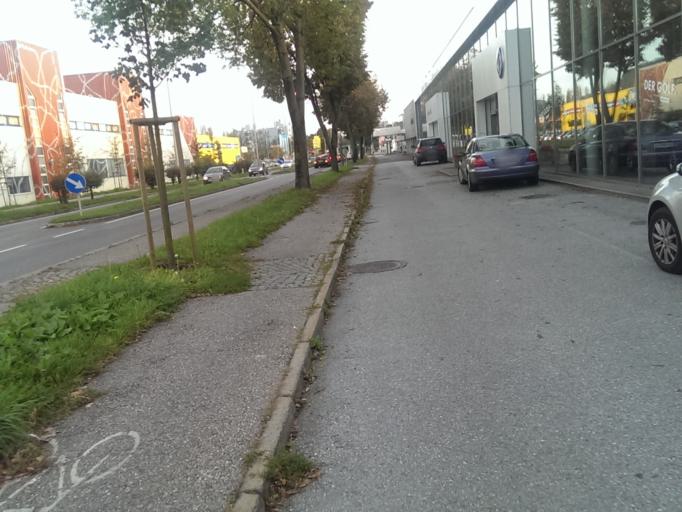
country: AT
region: Styria
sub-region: Graz Stadt
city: Goesting
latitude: 47.1032
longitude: 15.4147
